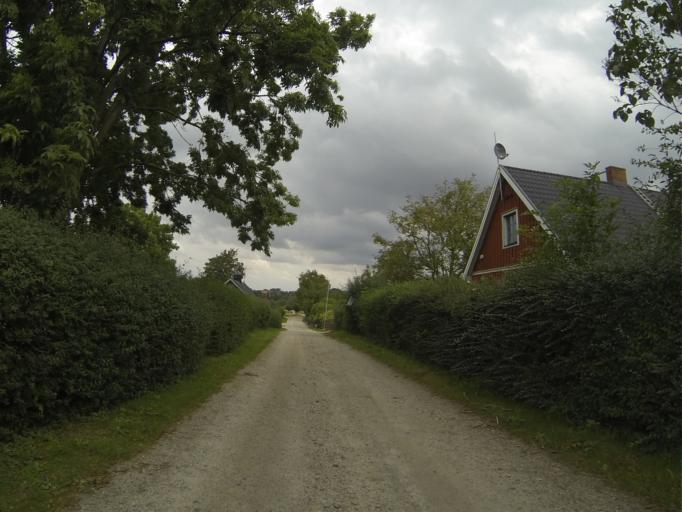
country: SE
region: Skane
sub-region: Lunds Kommun
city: Lund
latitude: 55.7826
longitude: 13.2058
